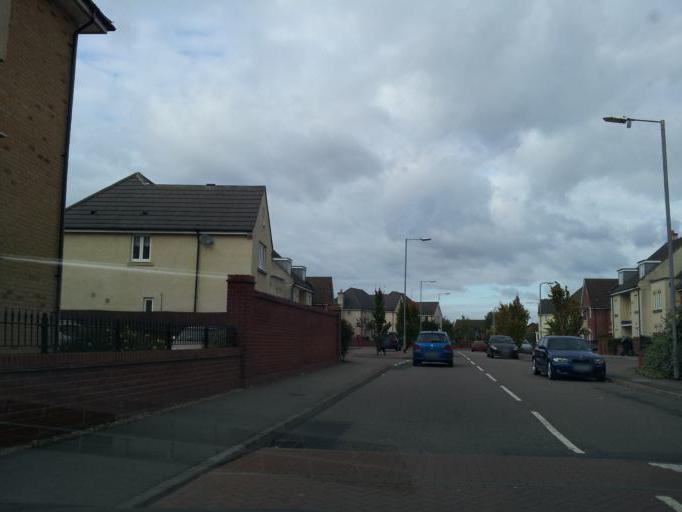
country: GB
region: England
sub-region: Northamptonshire
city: Bugbrooke
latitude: 52.2481
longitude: -0.9631
